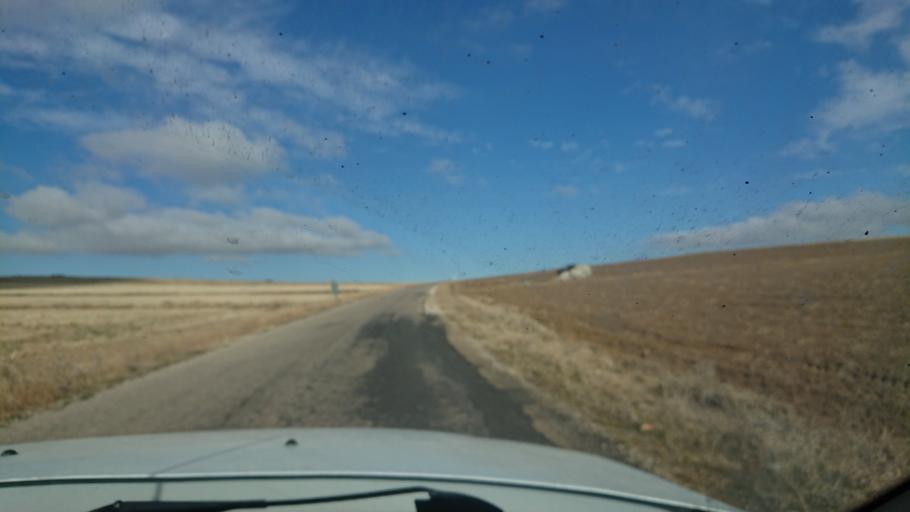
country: TR
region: Aksaray
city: Agacoren
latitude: 38.8350
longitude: 33.9548
